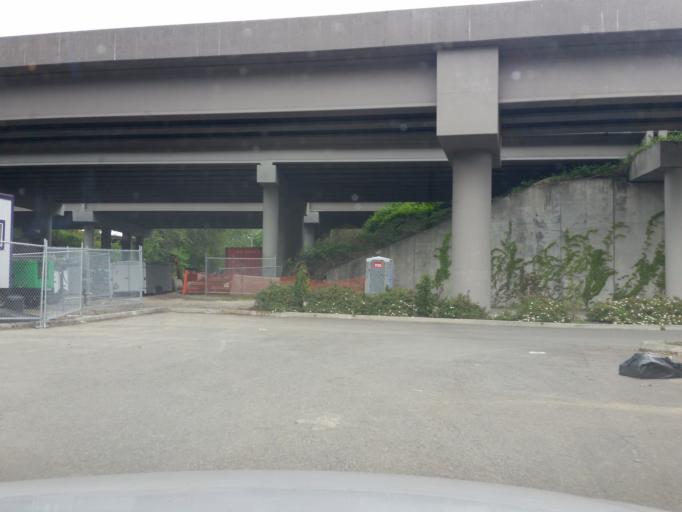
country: US
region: Washington
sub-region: King County
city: Bellevue
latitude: 47.6314
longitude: -122.1839
